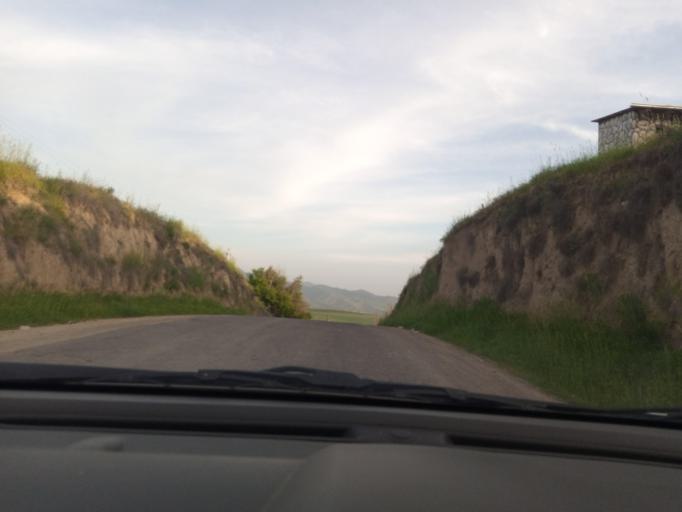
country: UZ
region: Toshkent
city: Parkent
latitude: 41.2354
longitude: 69.7373
